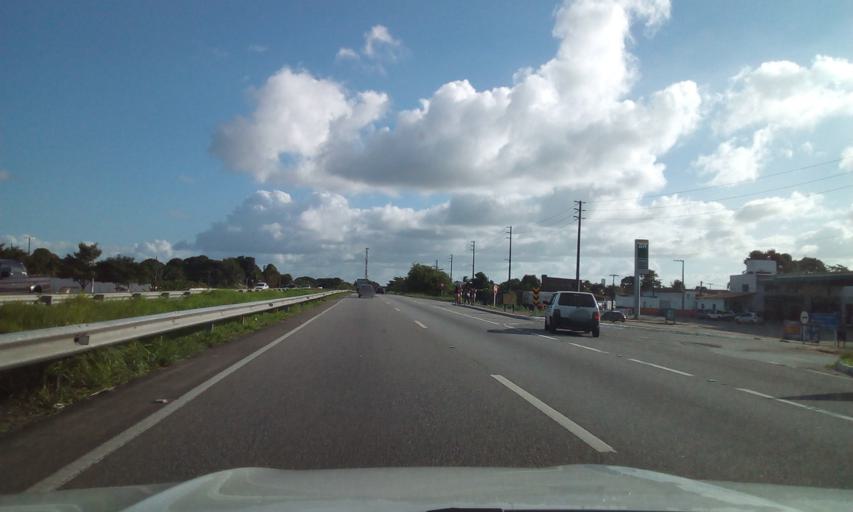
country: BR
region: Paraiba
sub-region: Bayeux
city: Bayeux
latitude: -7.1281
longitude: -34.9520
